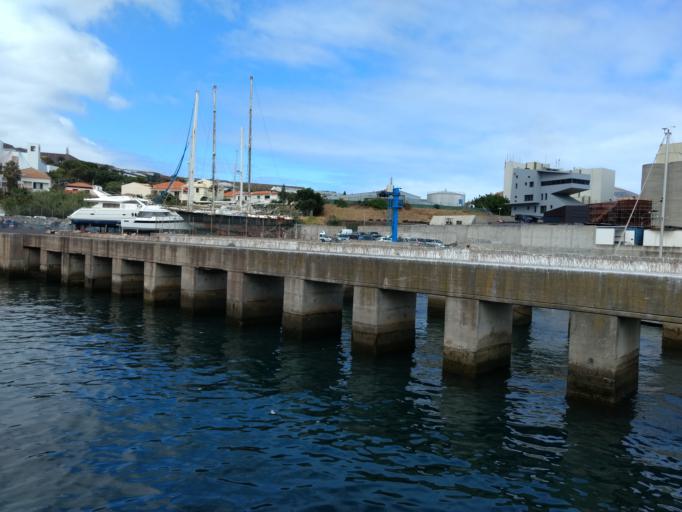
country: PT
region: Madeira
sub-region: Machico
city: Canical
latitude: 32.7366
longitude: -16.7353
